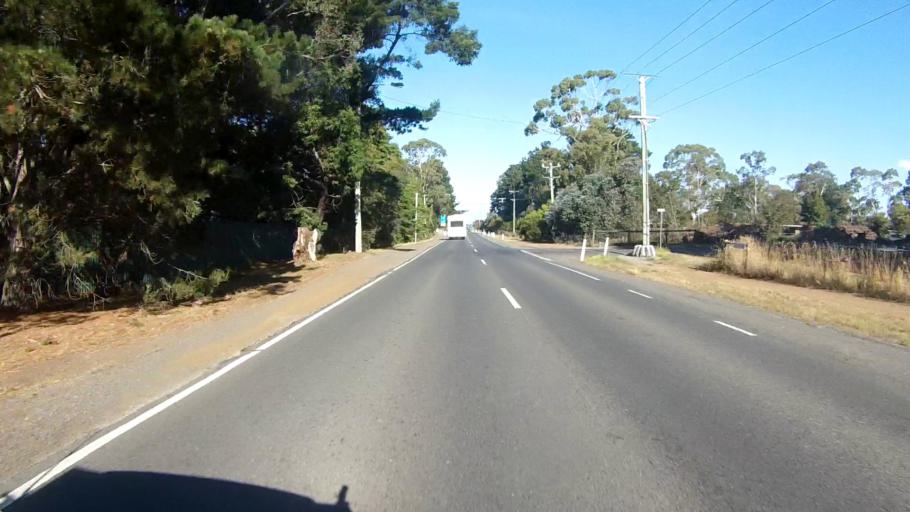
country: AU
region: Tasmania
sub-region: Clarence
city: Cambridge
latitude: -42.8377
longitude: 147.4639
